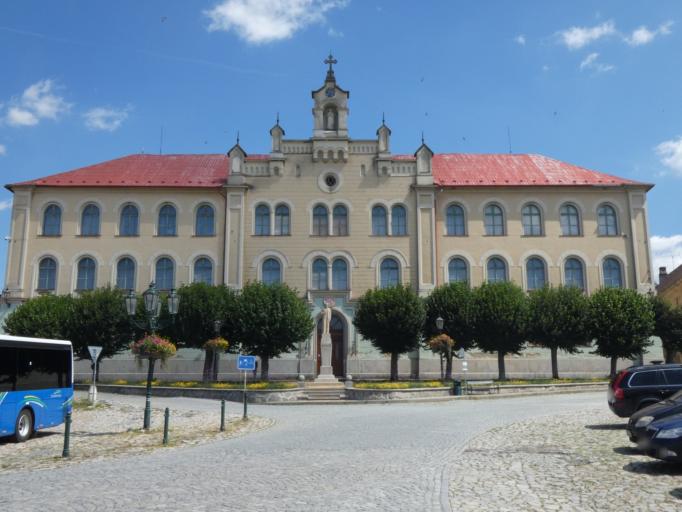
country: CZ
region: Plzensky
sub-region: Okres Plzen-Jih
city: Nepomuk
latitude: 49.4857
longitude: 13.5819
